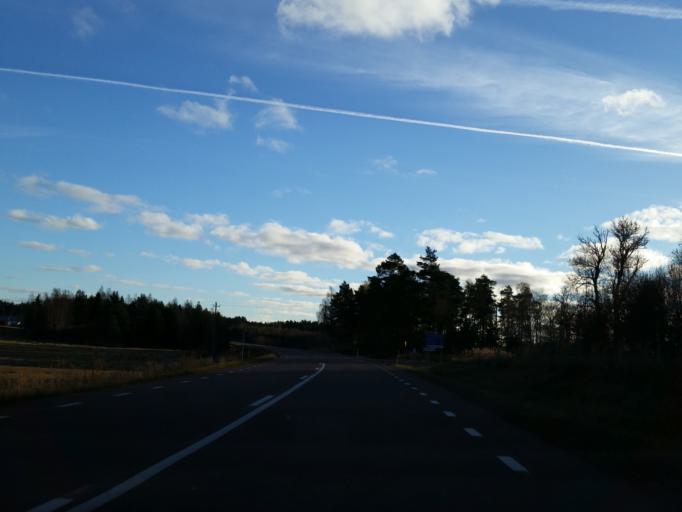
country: AX
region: Alands landsbygd
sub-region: Finstroem
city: Finstroem
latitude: 60.2773
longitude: 19.9515
